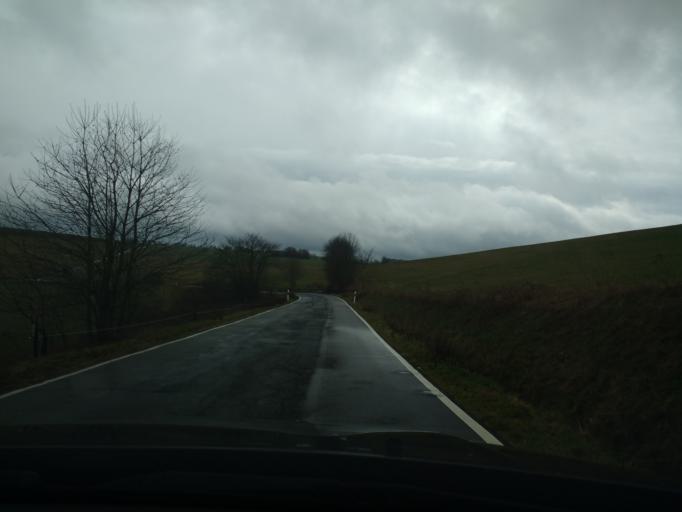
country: DE
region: Rheinland-Pfalz
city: Franzenheim
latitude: 49.6754
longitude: 6.6992
